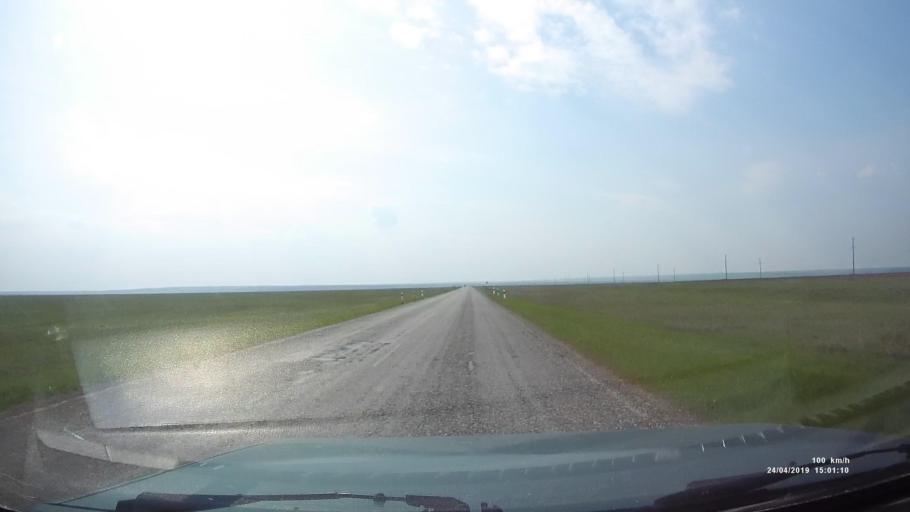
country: RU
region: Rostov
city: Remontnoye
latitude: 46.5656
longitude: 43.5396
